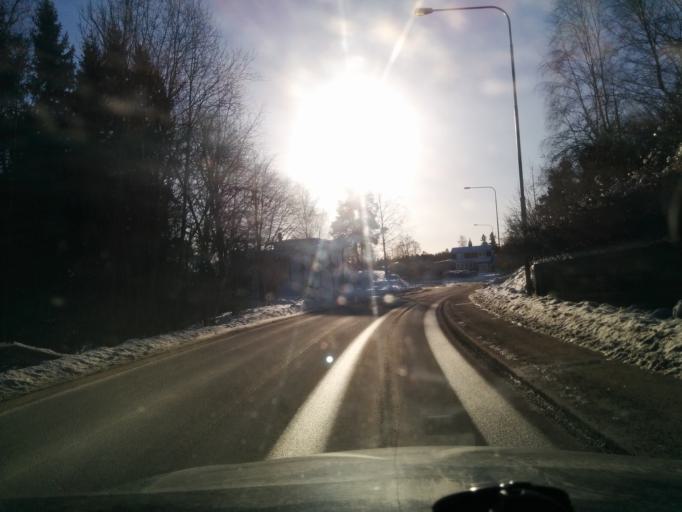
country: SE
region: Stockholm
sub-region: Taby Kommun
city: Taby
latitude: 59.4607
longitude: 18.0873
